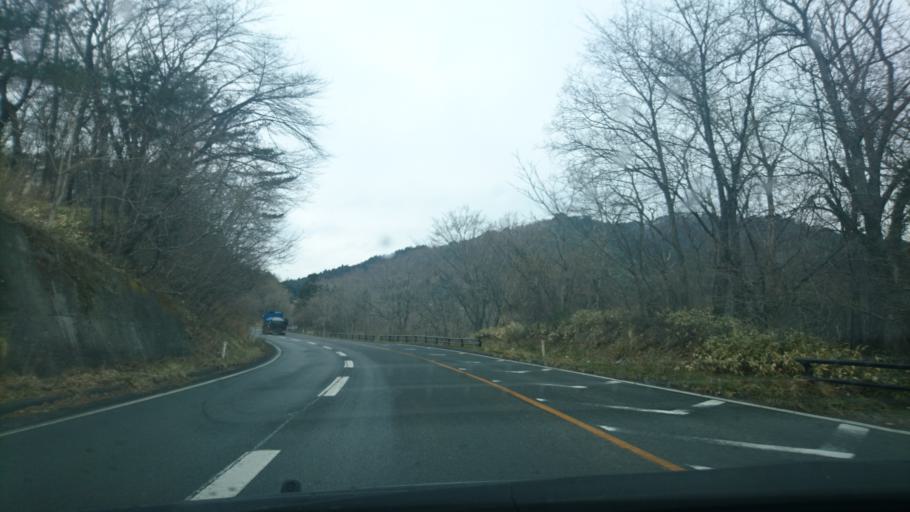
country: JP
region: Iwate
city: Ofunato
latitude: 39.0244
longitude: 141.6952
